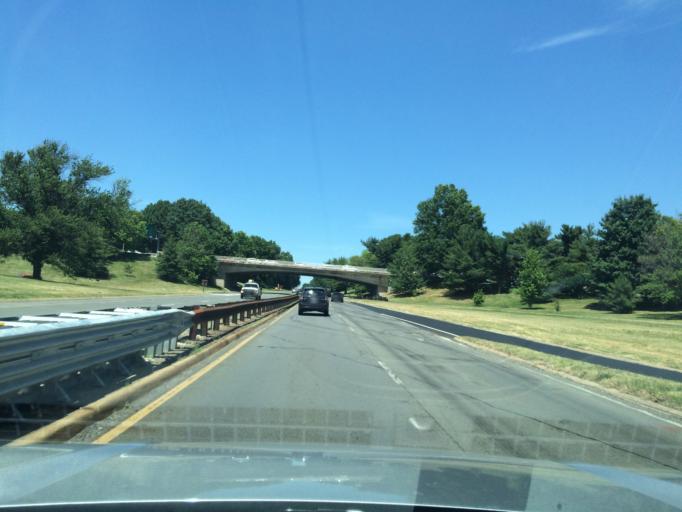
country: US
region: Virginia
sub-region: City of Alexandria
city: Alexandria
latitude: 38.8479
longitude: -77.0484
